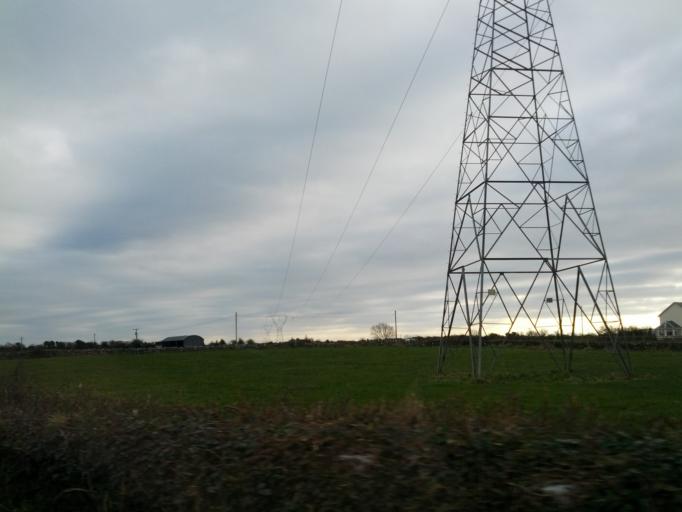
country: IE
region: Connaught
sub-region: County Galway
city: Oranmore
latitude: 53.1702
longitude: -8.8870
